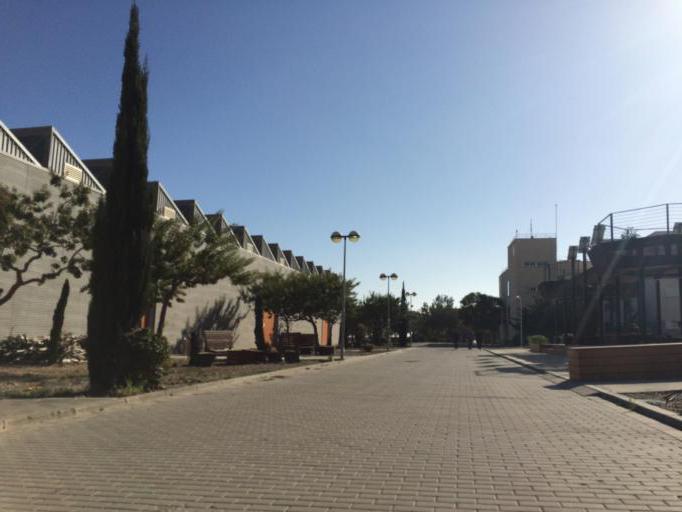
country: ES
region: Andalusia
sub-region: Provincia de Almeria
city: Almeria
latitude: 36.8297
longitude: -2.4065
